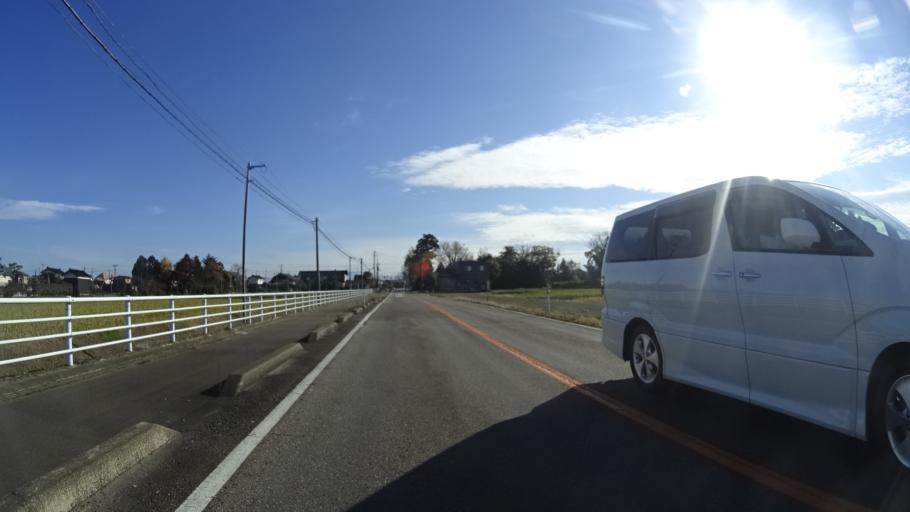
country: JP
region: Niigata
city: Mitsuke
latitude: 37.5548
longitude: 138.8530
